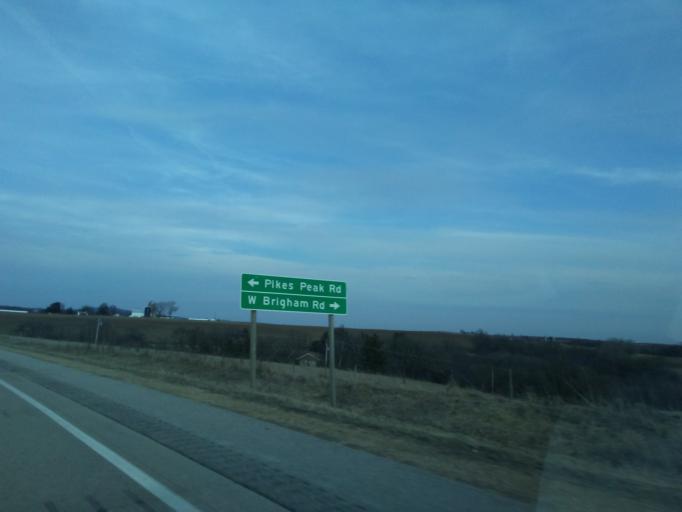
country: US
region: Wisconsin
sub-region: Iowa County
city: Barneveld
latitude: 43.0062
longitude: -89.9586
